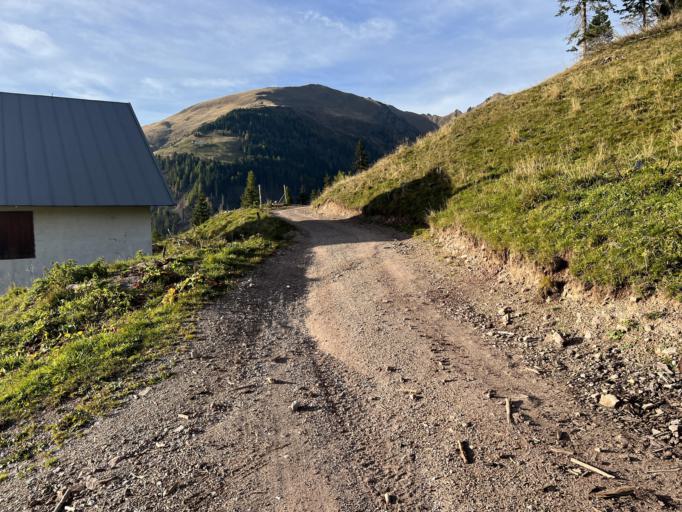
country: IT
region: Veneto
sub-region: Provincia di Belluno
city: Granvilla
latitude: 46.6314
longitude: 12.6876
